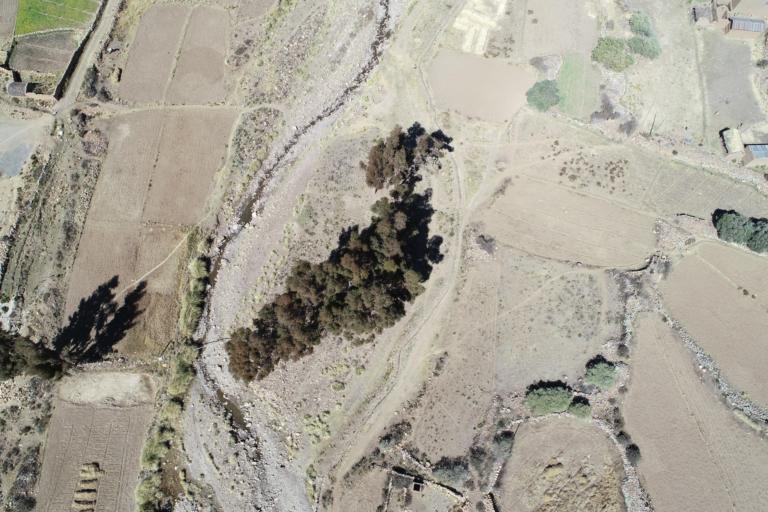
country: BO
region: La Paz
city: Achacachi
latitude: -15.8886
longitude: -68.8136
